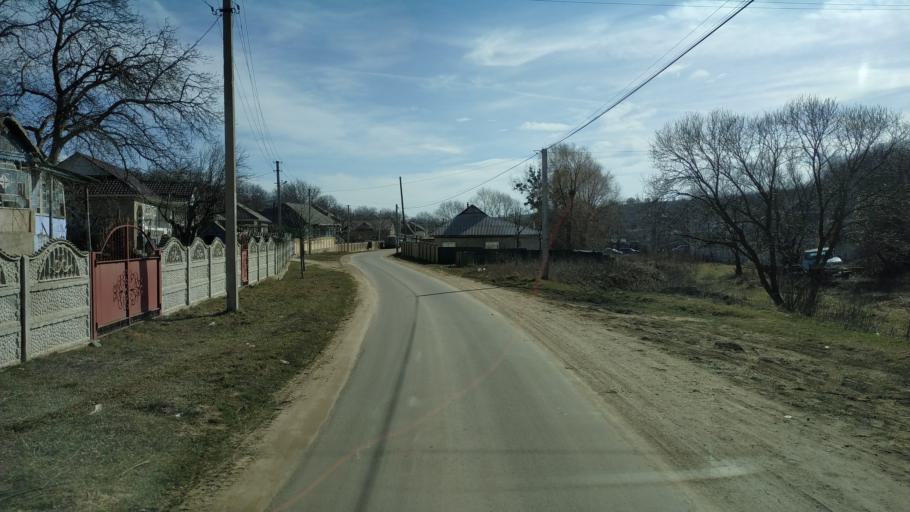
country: MD
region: Nisporeni
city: Nisporeni
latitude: 47.0970
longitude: 28.2951
